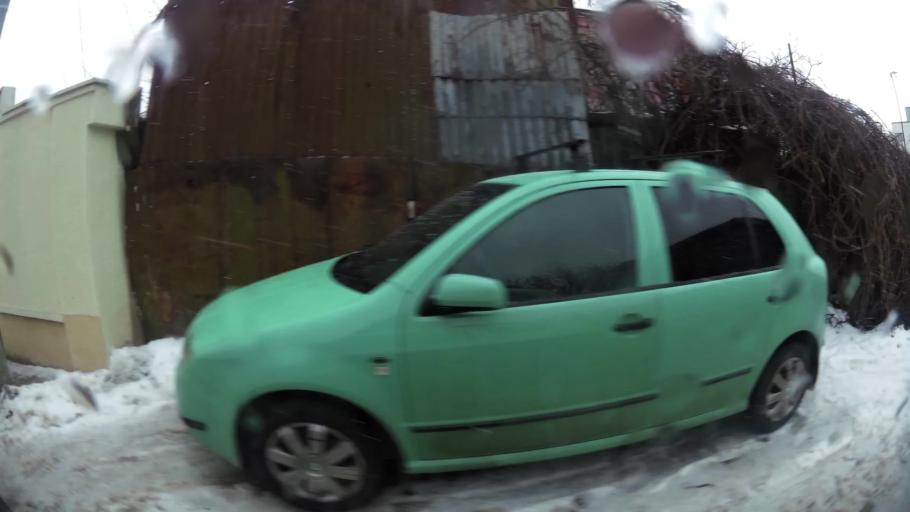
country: RO
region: Ilfov
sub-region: Comuna Chiajna
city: Rosu
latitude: 44.4292
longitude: 26.0057
